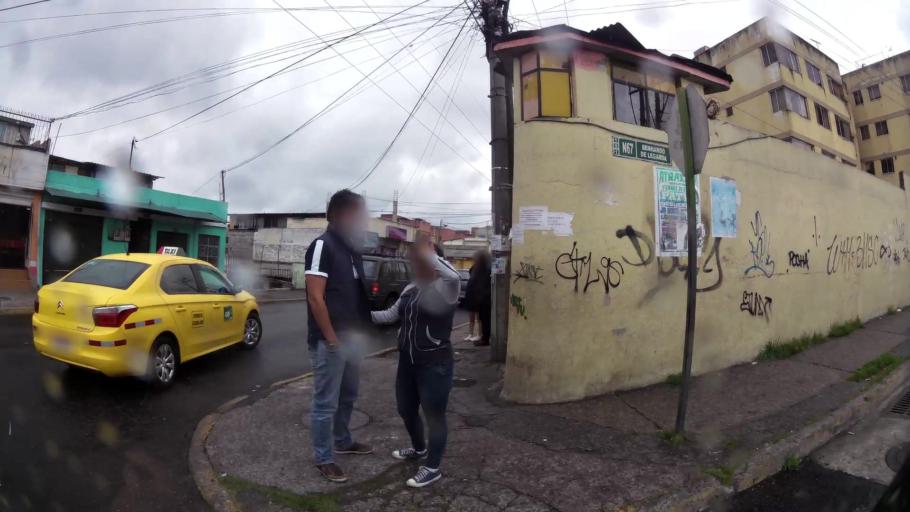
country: EC
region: Pichincha
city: Quito
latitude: -0.1147
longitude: -78.4996
